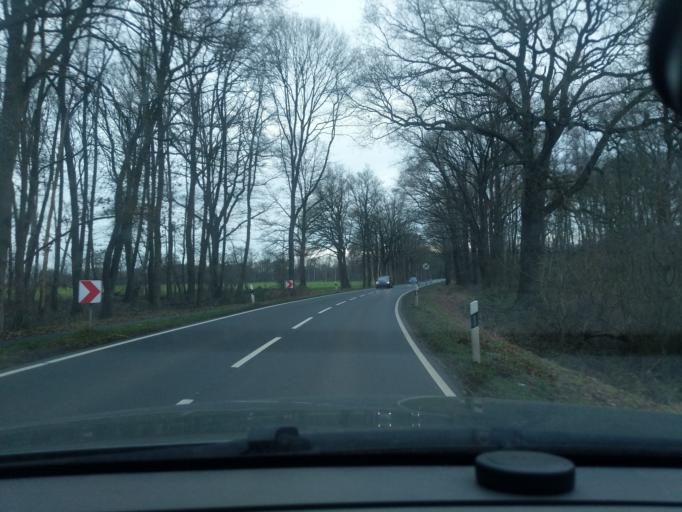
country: DE
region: Lower Saxony
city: Scheessel
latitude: 53.1867
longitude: 9.4866
